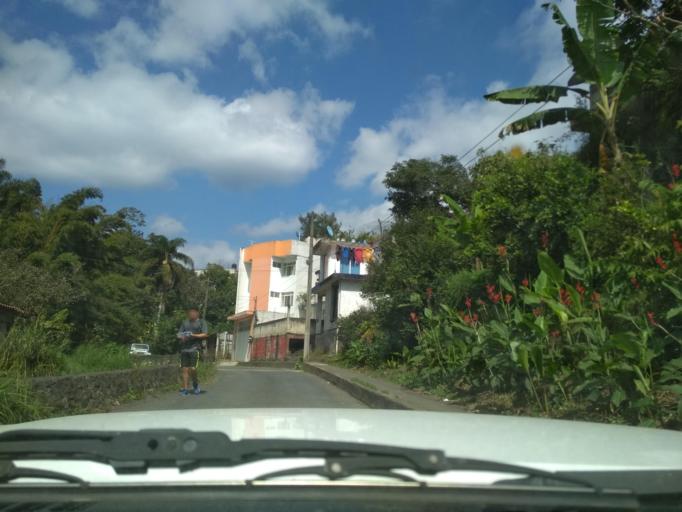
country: MX
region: Veracruz
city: Coatepec
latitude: 19.4543
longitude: -96.9521
